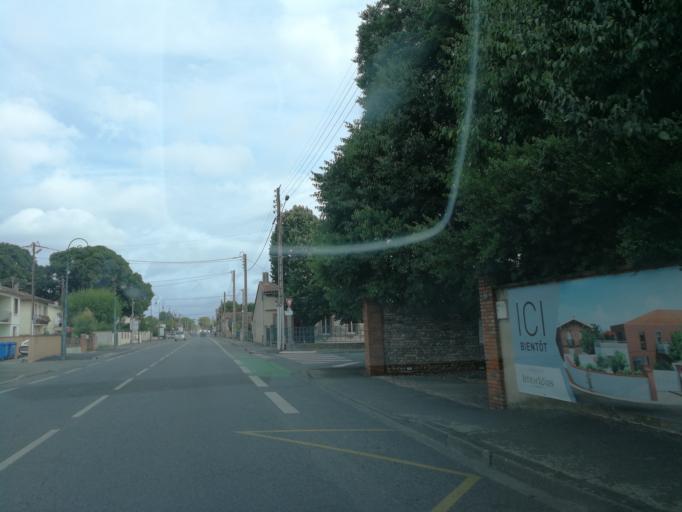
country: FR
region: Midi-Pyrenees
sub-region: Departement de la Haute-Garonne
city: Aucamville
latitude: 43.6717
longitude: 1.4270
